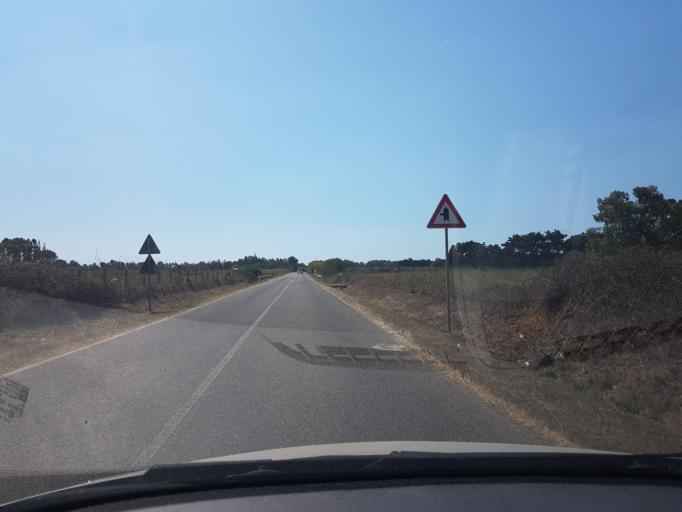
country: IT
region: Sardinia
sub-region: Provincia di Oristano
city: Riola Sardo
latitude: 39.9981
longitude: 8.4879
